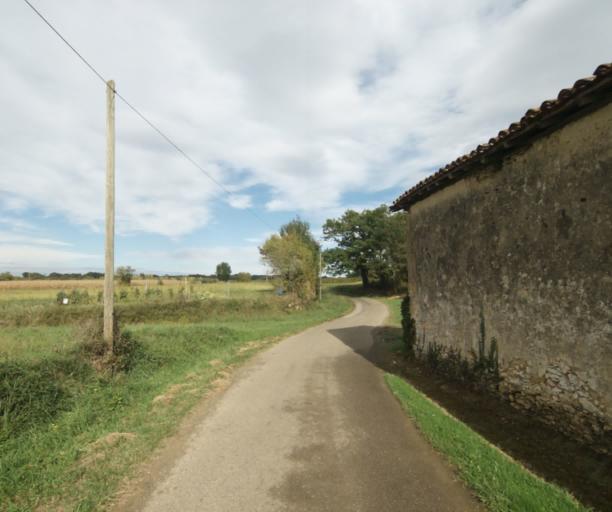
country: FR
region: Midi-Pyrenees
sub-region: Departement du Gers
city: Cazaubon
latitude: 43.8782
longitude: -0.1409
